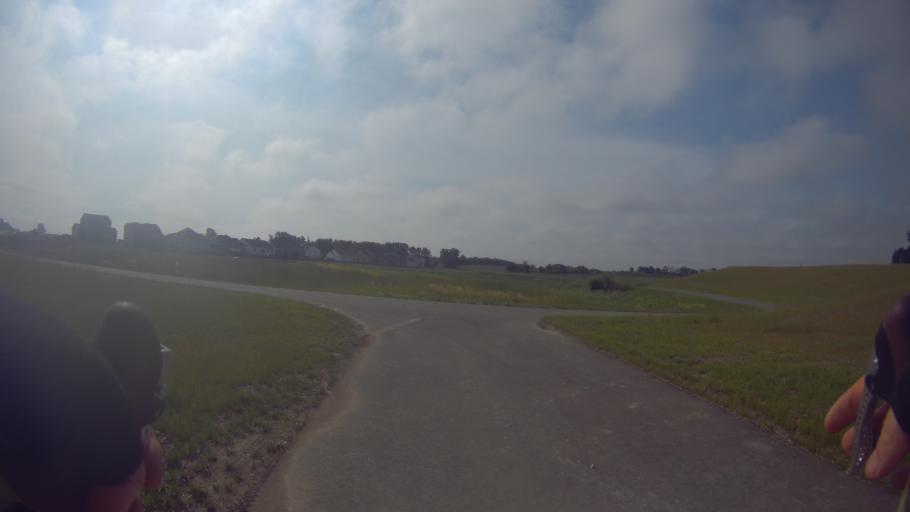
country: US
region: Wisconsin
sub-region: Dane County
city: McFarland
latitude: 43.0185
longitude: -89.2758
